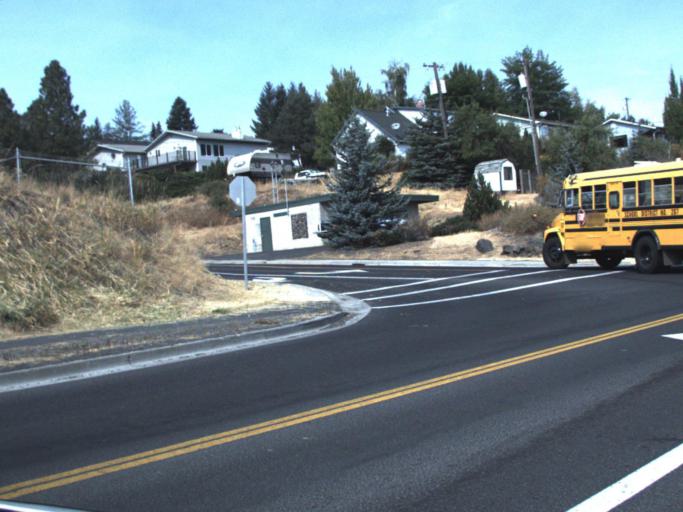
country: US
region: Washington
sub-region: Whitman County
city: Pullman
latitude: 46.7472
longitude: -117.1724
